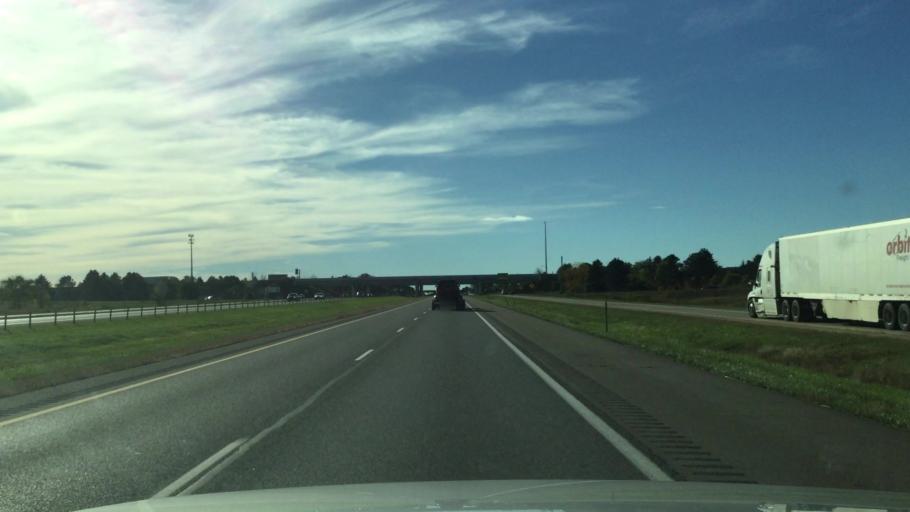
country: US
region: Michigan
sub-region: Calhoun County
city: Marshall
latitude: 42.2975
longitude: -84.9911
